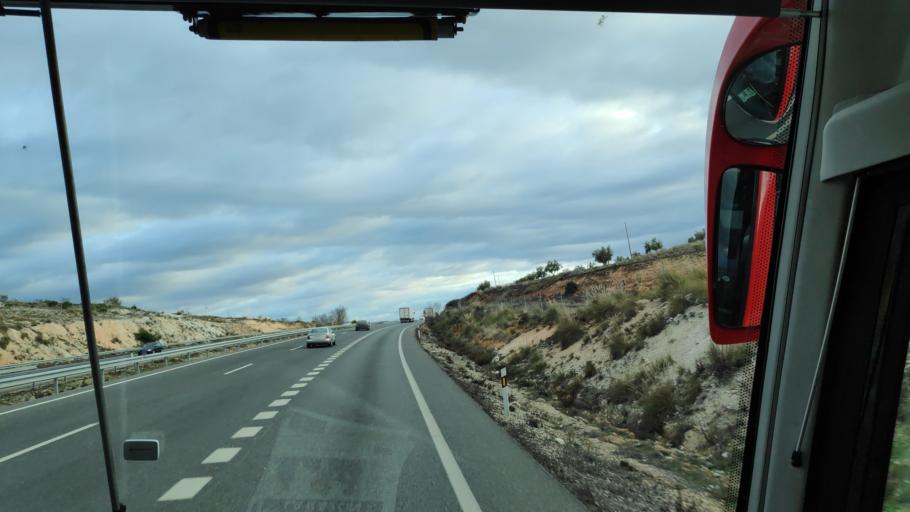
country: ES
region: Madrid
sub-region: Provincia de Madrid
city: Villarejo de Salvanes
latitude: 40.1905
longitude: -3.2998
